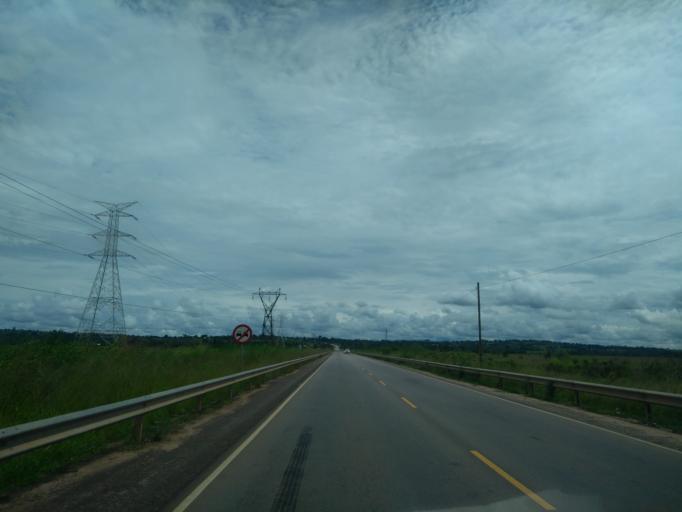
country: UG
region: Central Region
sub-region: Gomba District
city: Kanoni
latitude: -0.0315
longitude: 32.0111
